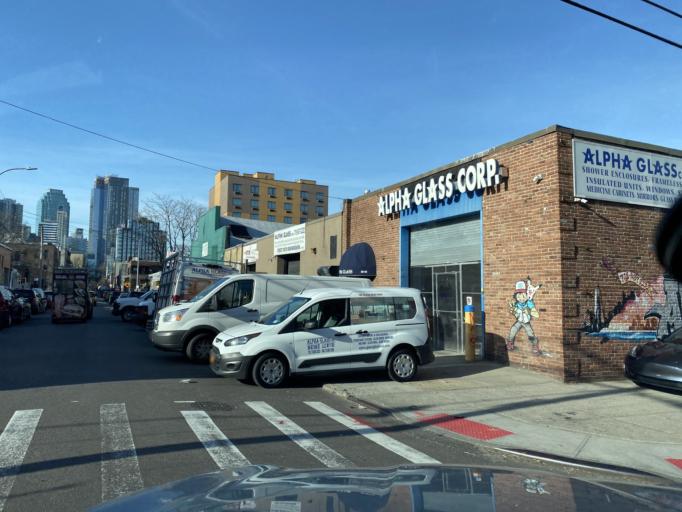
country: US
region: New York
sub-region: Queens County
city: Long Island City
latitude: 40.7562
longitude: -73.9367
